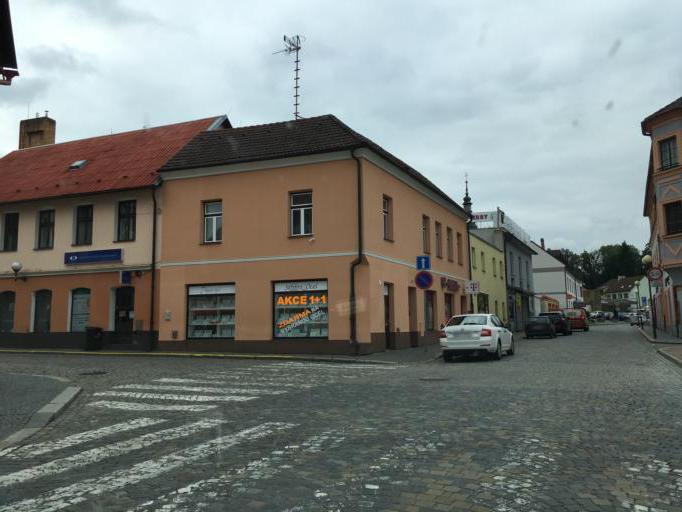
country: CZ
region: Vysocina
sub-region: Okres Pelhrimov
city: Pelhrimov
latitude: 49.4325
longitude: 15.2245
